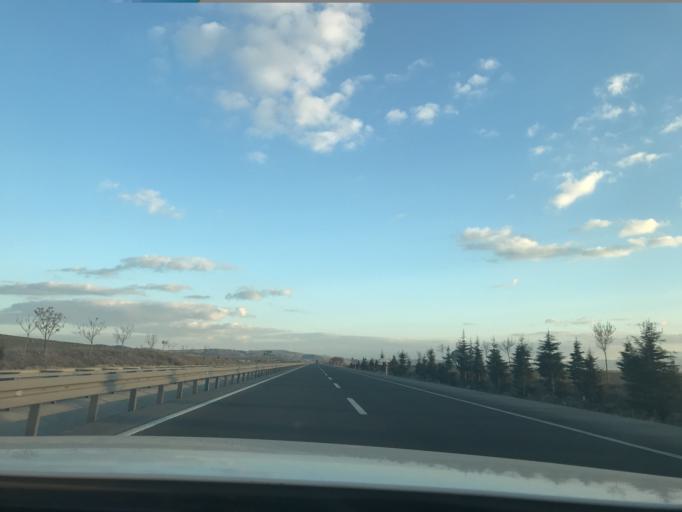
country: TR
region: Ankara
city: Yenice
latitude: 39.4036
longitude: 32.8737
